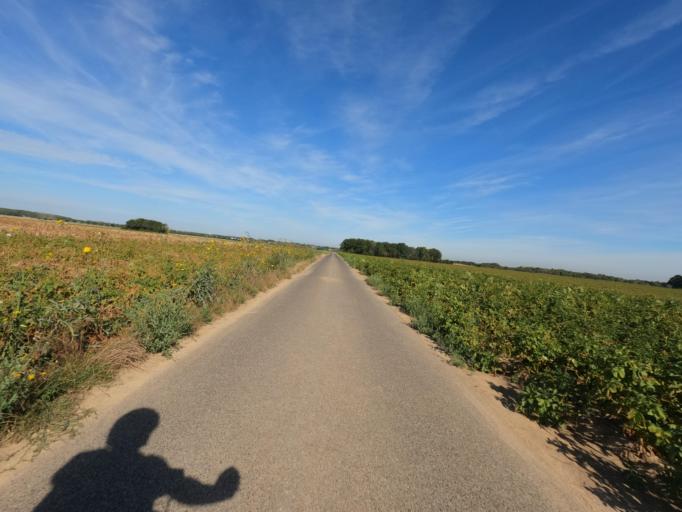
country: DE
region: North Rhine-Westphalia
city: Erkelenz
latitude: 51.0461
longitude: 6.3662
